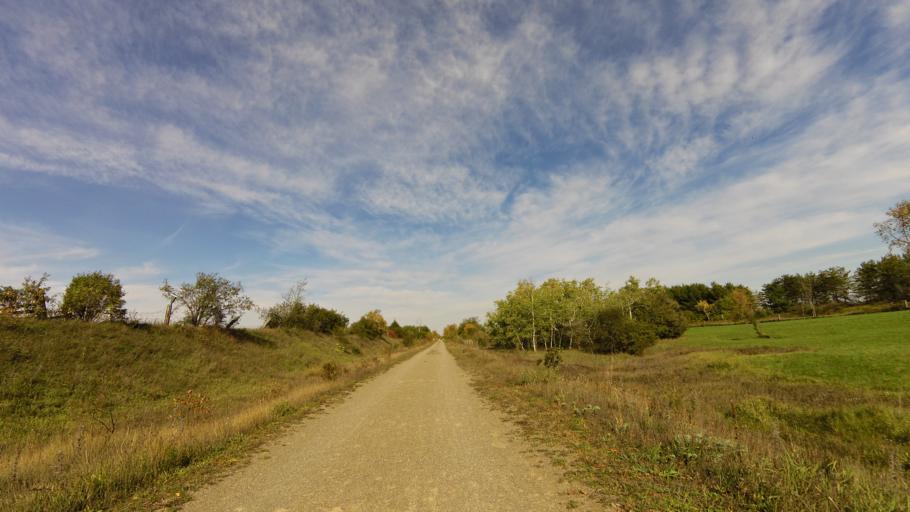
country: CA
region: Ontario
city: Orangeville
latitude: 43.7909
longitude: -80.0501
